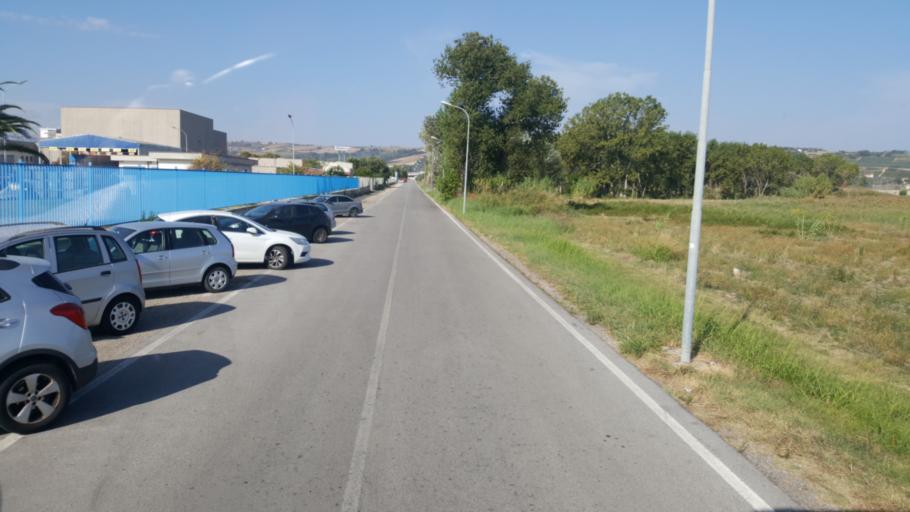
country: IT
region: Molise
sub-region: Provincia di Campobasso
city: Portocannone
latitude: 41.9457
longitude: 15.0057
